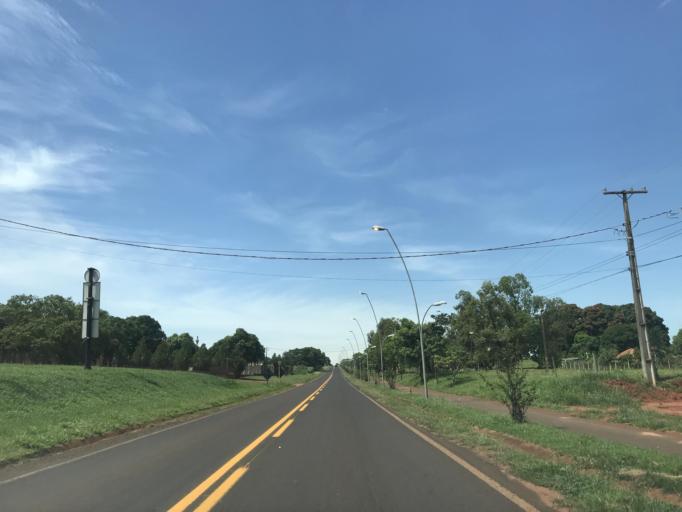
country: BR
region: Parana
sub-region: Terra Rica
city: Terra Rica
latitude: -22.7426
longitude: -52.6249
